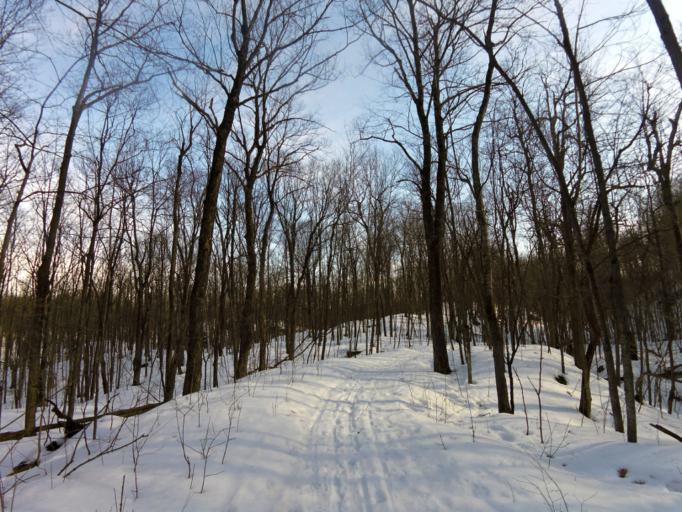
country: CA
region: Quebec
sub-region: Outaouais
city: Gatineau
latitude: 45.4734
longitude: -75.7964
